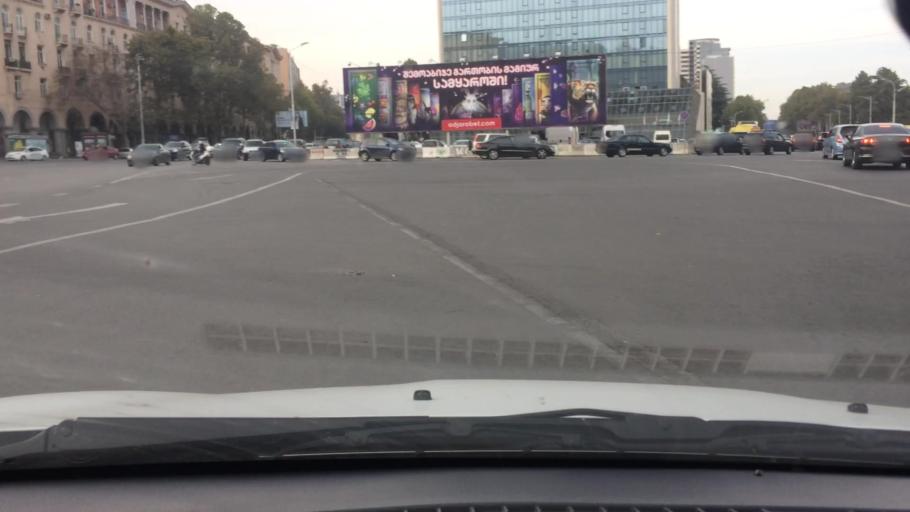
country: GE
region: T'bilisi
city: Tbilisi
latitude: 41.7176
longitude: 44.7787
